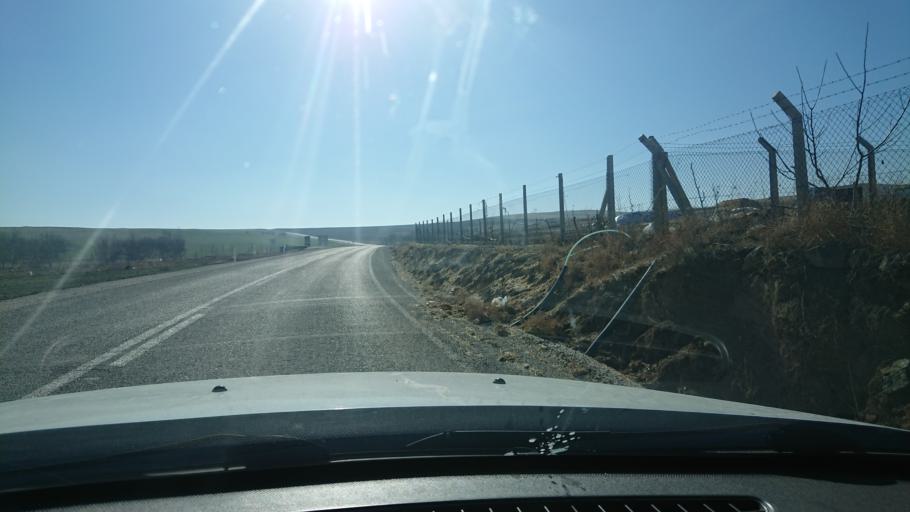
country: TR
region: Aksaray
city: Agacoren
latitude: 38.9182
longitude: 33.9288
